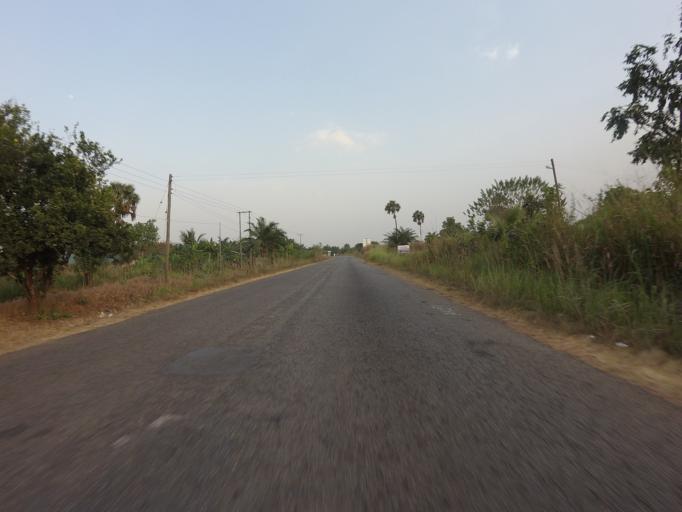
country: GH
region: Volta
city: Ho
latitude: 6.5710
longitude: 0.3888
